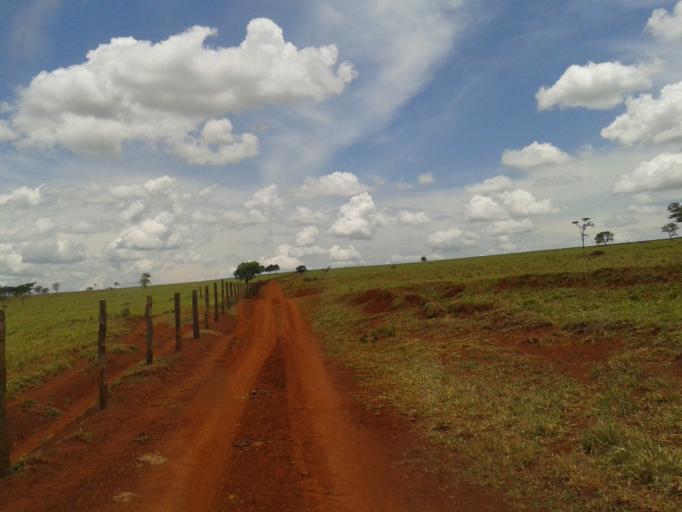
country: BR
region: Minas Gerais
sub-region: Centralina
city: Centralina
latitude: -18.7062
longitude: -49.2248
